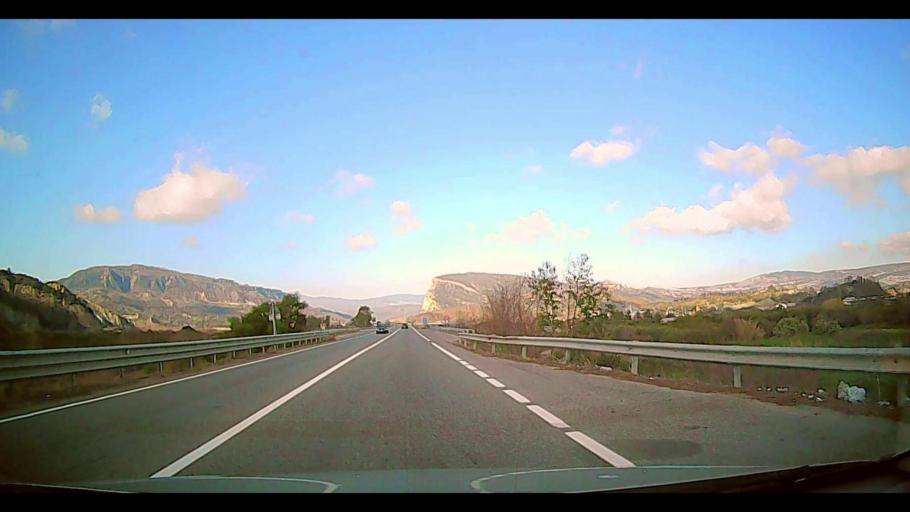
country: IT
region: Calabria
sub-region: Provincia di Crotone
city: Santa Severina
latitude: 39.1788
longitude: 16.9231
